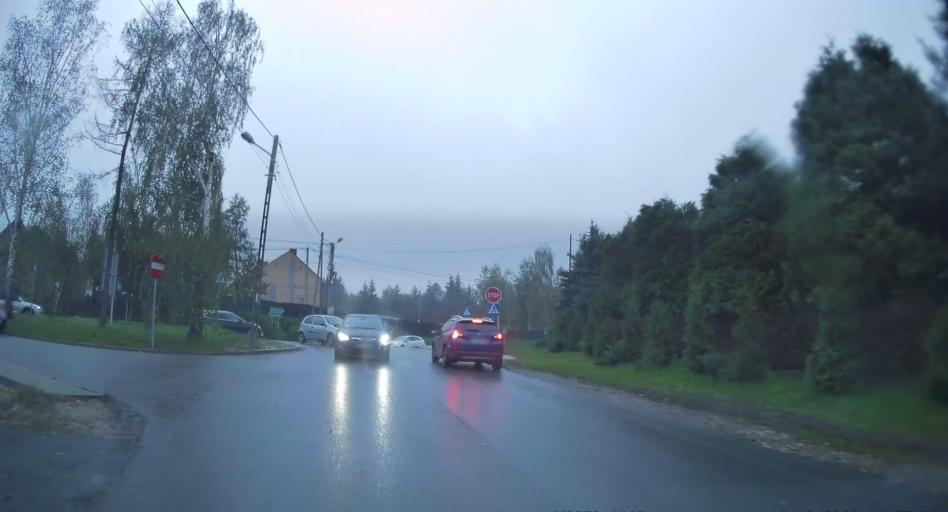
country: PL
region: Lesser Poland Voivodeship
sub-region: Powiat krakowski
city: Ochojno
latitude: 49.9735
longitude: 20.0005
